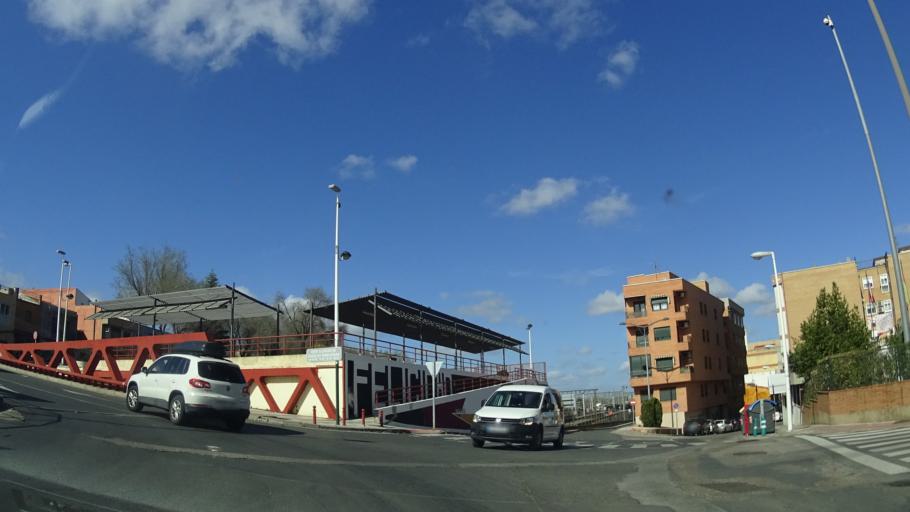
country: ES
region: Castille-La Mancha
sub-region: Provincia de Ciudad Real
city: Puertollano
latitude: 38.6872
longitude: -4.1130
